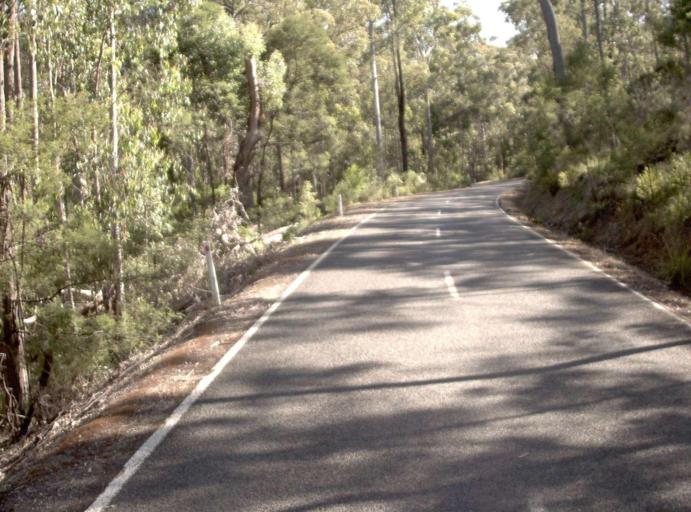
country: AU
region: Victoria
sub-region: East Gippsland
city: Lakes Entrance
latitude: -37.6118
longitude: 148.5126
